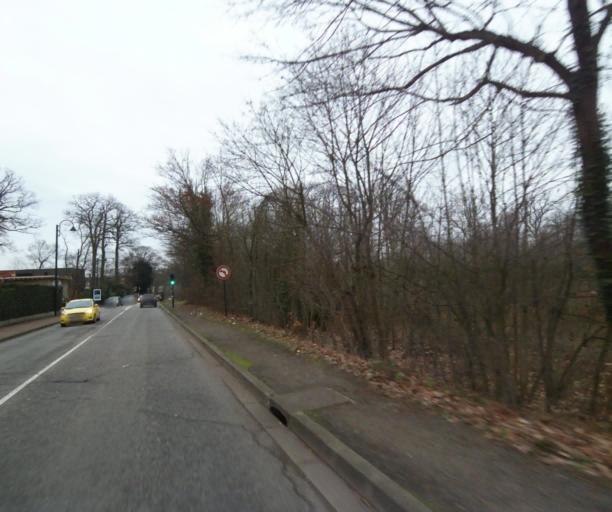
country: FR
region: Ile-de-France
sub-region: Departement des Yvelines
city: La Celle-Saint-Cloud
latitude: 48.8414
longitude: 2.1457
